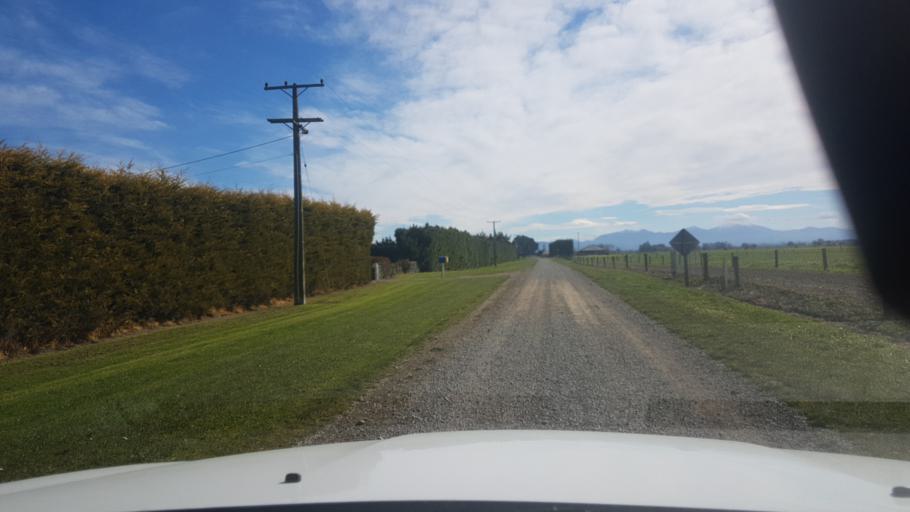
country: NZ
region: Canterbury
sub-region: Timaru District
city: Timaru
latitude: -44.2493
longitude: 171.3843
